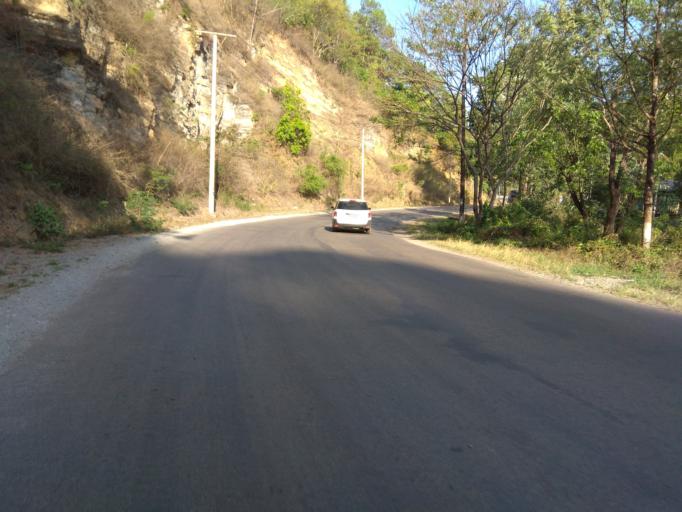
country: MM
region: Shan
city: Taunggyi
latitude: 20.6339
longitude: 96.5830
